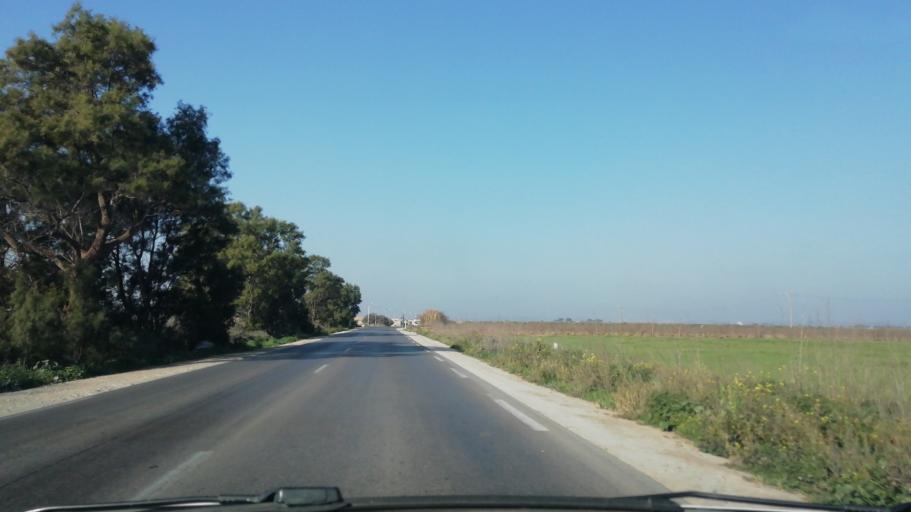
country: DZ
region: Mostaganem
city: Mostaganem
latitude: 35.7591
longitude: 0.0699
